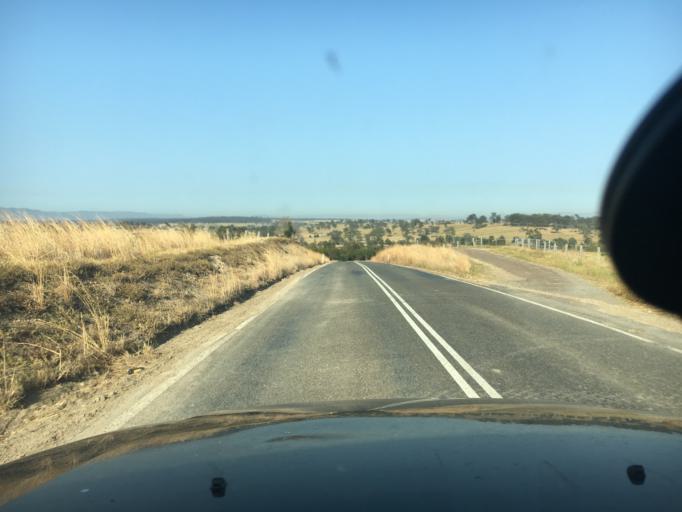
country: AU
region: New South Wales
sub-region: Cessnock
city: Branxton
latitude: -32.5848
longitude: 151.3138
